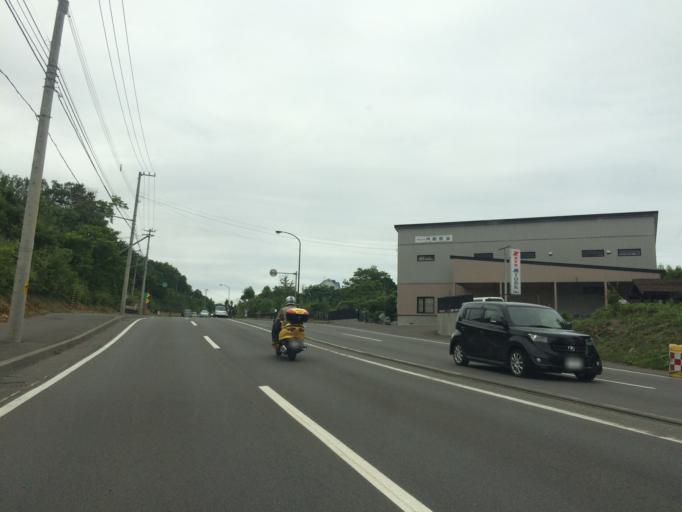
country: JP
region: Hokkaido
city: Otaru
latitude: 43.1457
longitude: 141.1409
